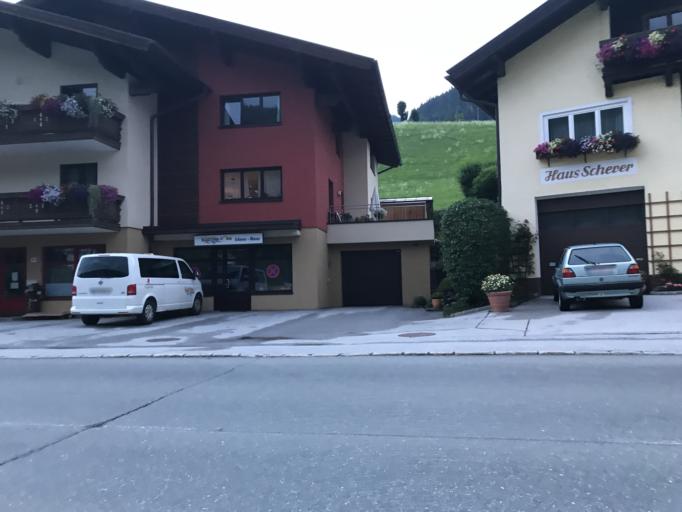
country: AT
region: Salzburg
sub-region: Politischer Bezirk Sankt Johann im Pongau
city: Wagrain
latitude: 47.3339
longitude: 13.2945
